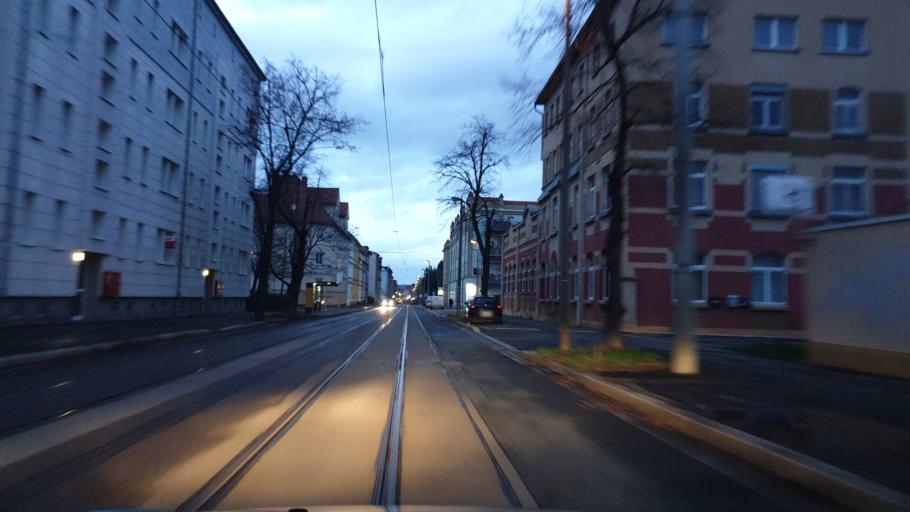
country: DE
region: Thuringia
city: Gera
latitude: 50.8584
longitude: 12.0729
